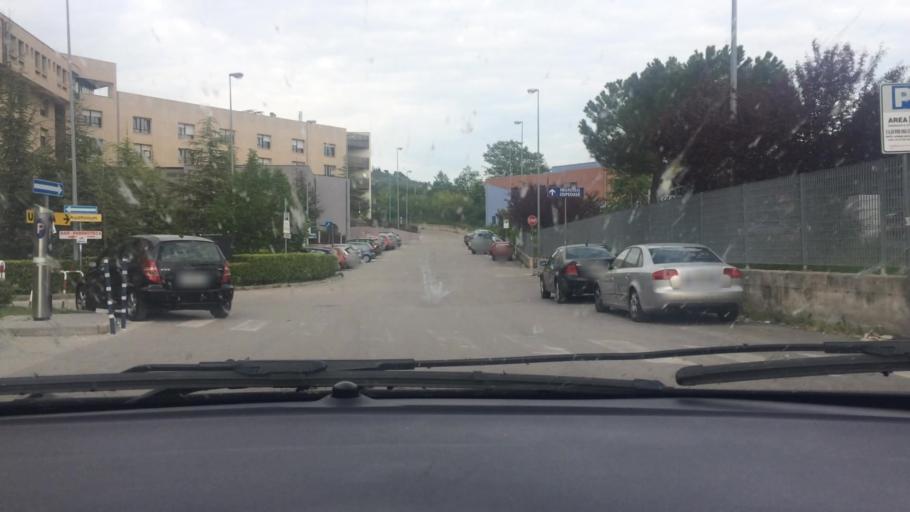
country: IT
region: Basilicate
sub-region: Provincia di Potenza
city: Potenza
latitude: 40.6509
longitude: 15.8064
